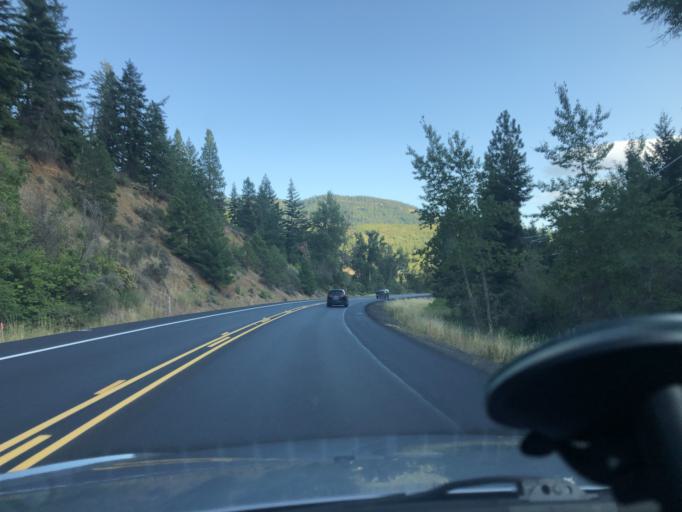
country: US
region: Washington
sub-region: Kittitas County
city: Cle Elum
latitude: 47.2121
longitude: -120.6987
